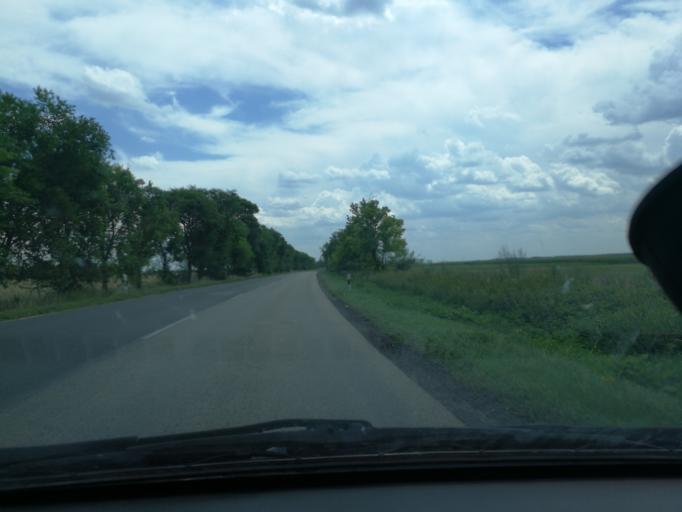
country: HU
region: Bacs-Kiskun
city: Apostag
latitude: 46.8583
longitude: 18.9921
